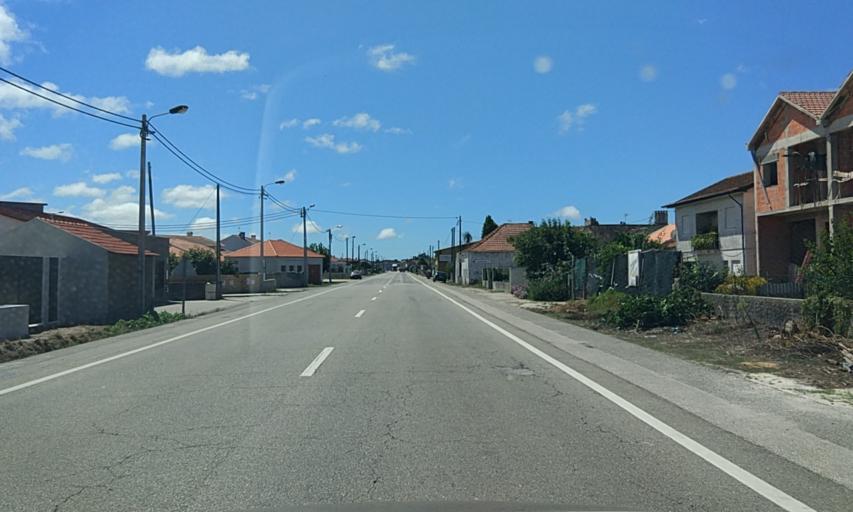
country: PT
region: Coimbra
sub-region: Mira
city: Mira
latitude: 40.4838
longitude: -8.6900
